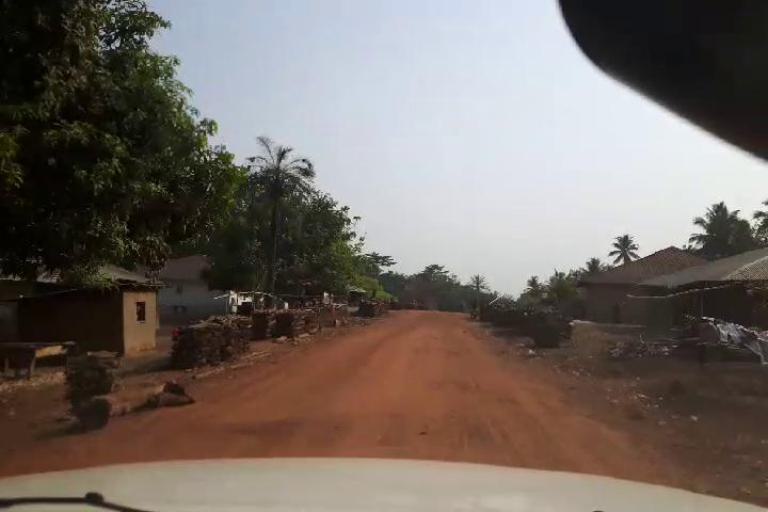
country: SL
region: Northern Province
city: Masingbi
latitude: 8.8247
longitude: -11.8561
